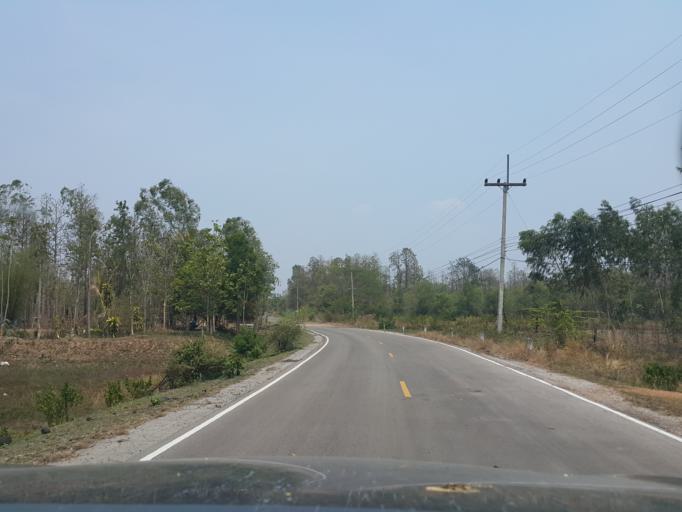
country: TH
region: Lampang
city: Mae Phrik
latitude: 17.5639
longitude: 99.0938
